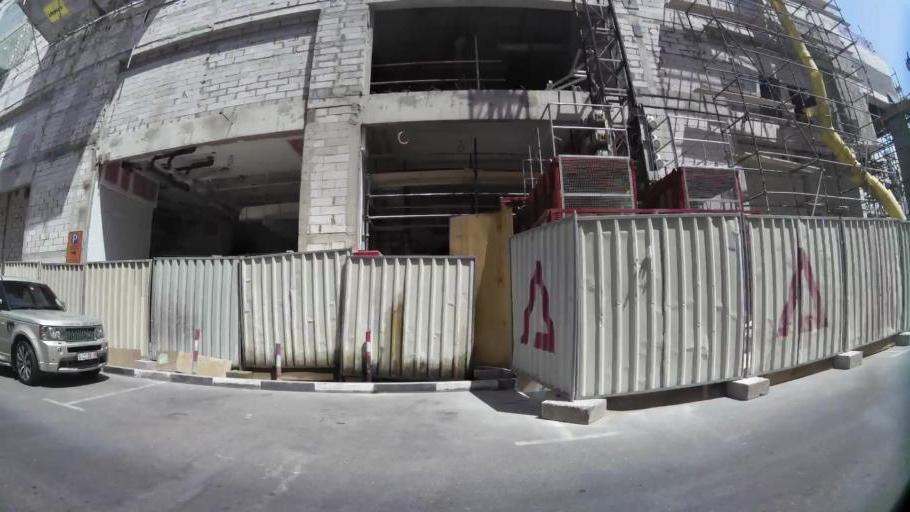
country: AE
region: Ash Shariqah
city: Sharjah
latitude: 25.2773
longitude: 55.3501
